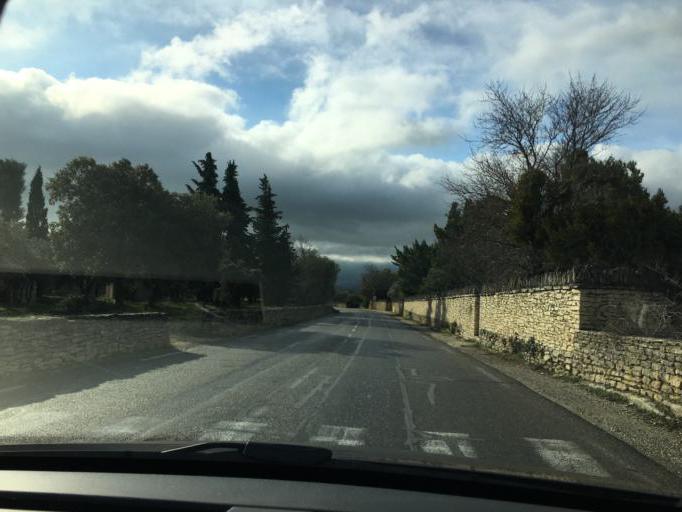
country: FR
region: Provence-Alpes-Cote d'Azur
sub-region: Departement du Vaucluse
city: Gordes
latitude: 43.9082
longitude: 5.1976
